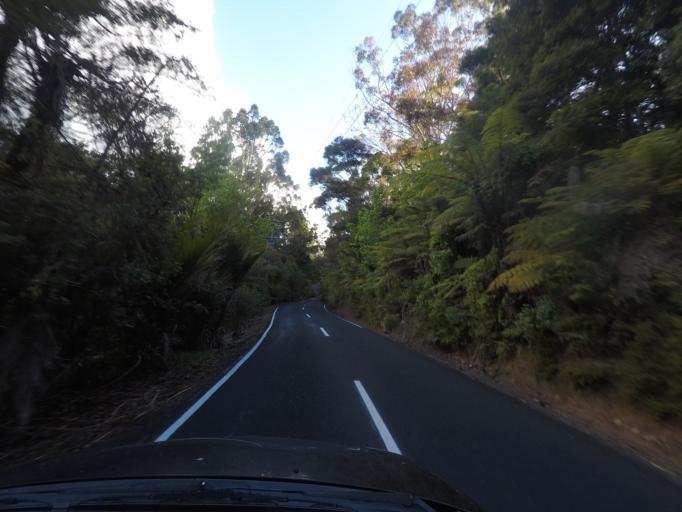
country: NZ
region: Auckland
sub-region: Auckland
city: Titirangi
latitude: -36.9325
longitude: 174.6194
